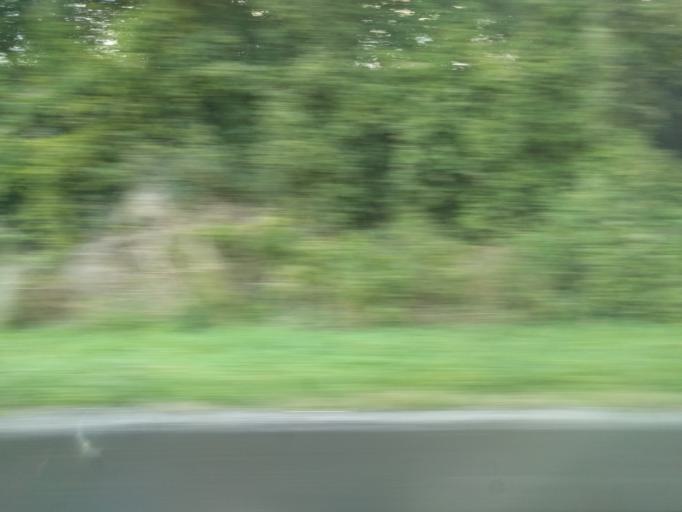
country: DK
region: Zealand
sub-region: Slagelse Kommune
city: Forlev
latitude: 55.3744
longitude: 11.2749
